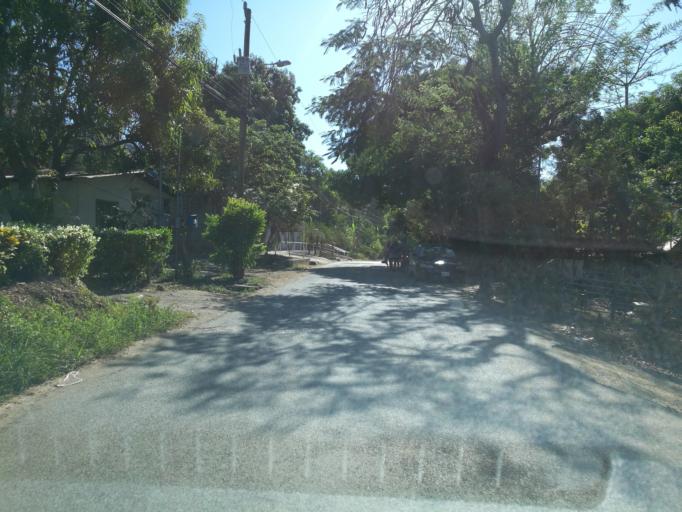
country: CR
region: Guanacaste
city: Juntas
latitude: 10.0994
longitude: -84.9913
